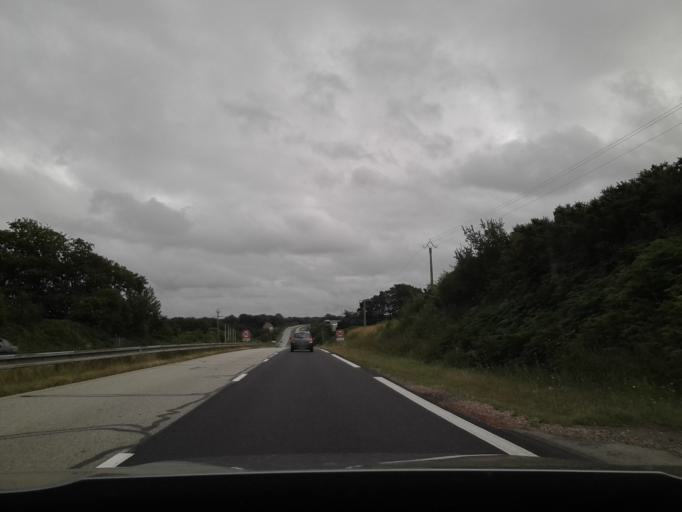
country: FR
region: Lower Normandy
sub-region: Departement de la Manche
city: La Glacerie
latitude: 49.5826
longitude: -1.5901
